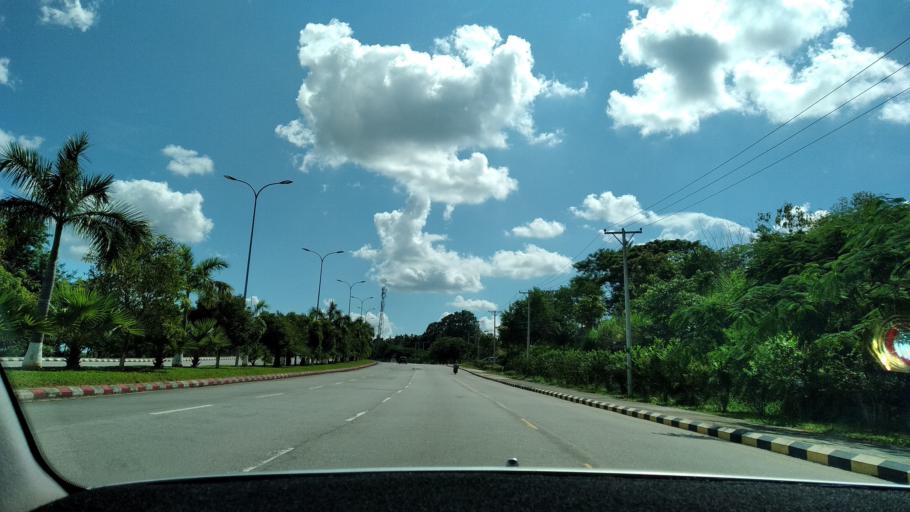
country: MM
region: Mandalay
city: Nay Pyi Taw
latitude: 19.7917
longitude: 96.1462
